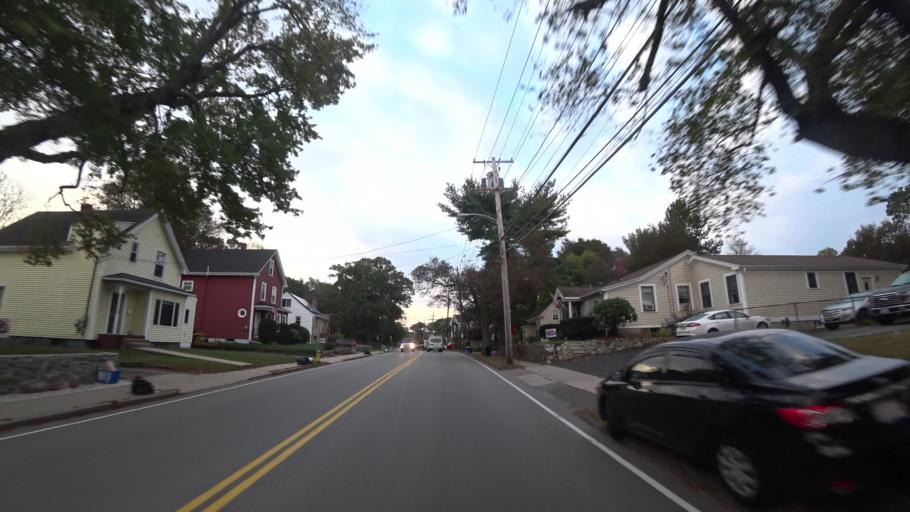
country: US
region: Massachusetts
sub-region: Essex County
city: Saugus
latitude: 42.4591
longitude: -71.0101
